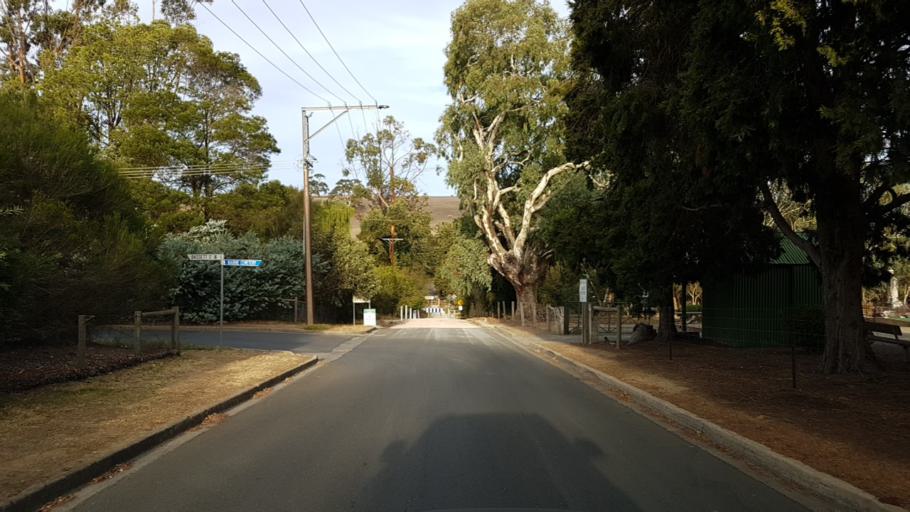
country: AU
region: South Australia
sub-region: Mount Barker
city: Nairne
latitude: -35.0327
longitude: 138.9099
